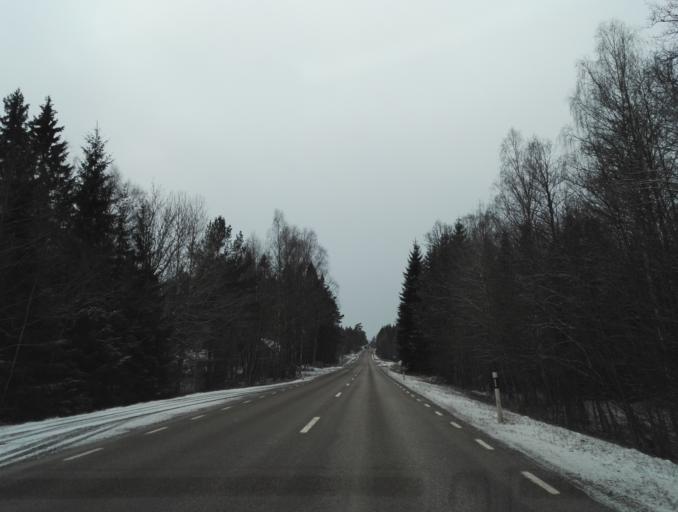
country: SE
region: Kalmar
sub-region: Hultsfreds Kommun
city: Virserum
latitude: 57.2670
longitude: 15.5646
